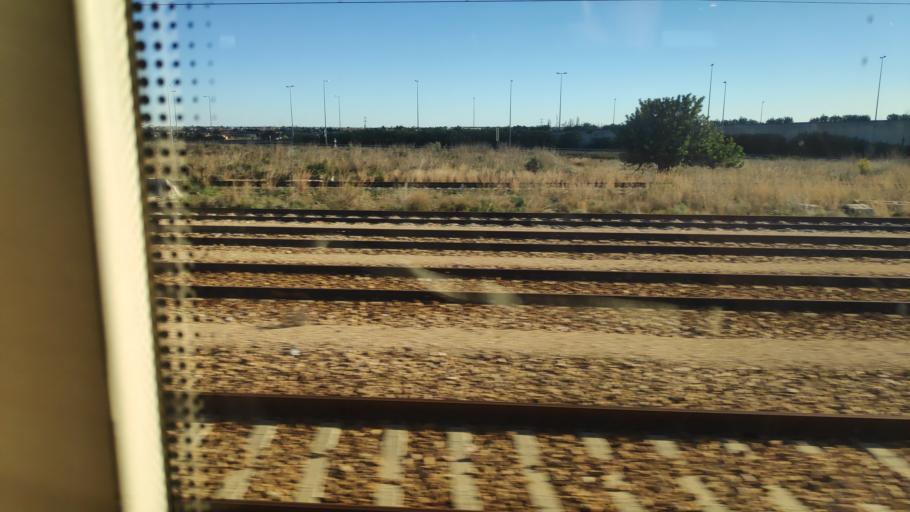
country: ES
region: Valencia
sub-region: Provincia de Castello
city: Castello de la Plana
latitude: 40.0237
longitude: -0.0010
